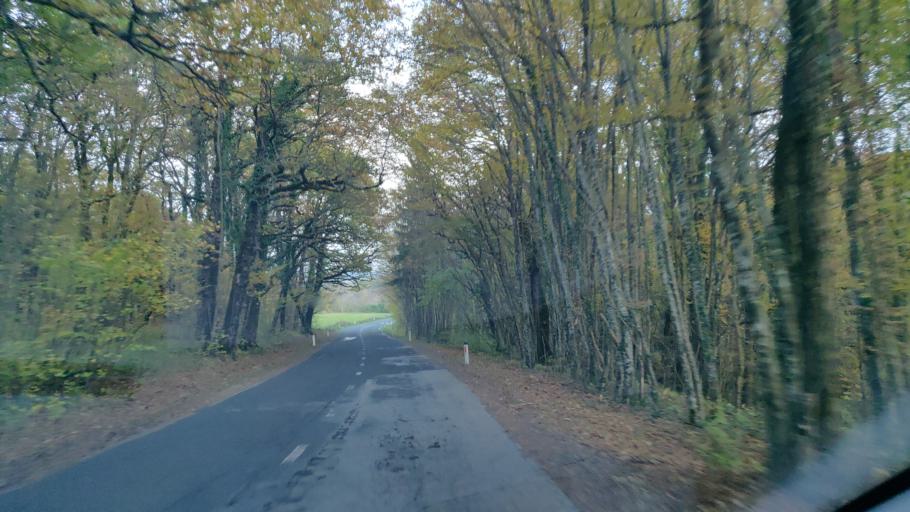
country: SI
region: Sezana
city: Sezana
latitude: 45.7660
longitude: 13.8897
